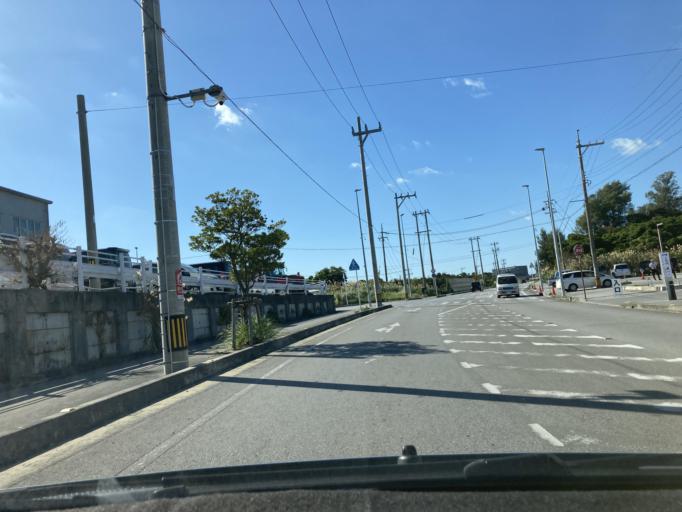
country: JP
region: Okinawa
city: Gushikawa
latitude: 26.3757
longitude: 127.8313
